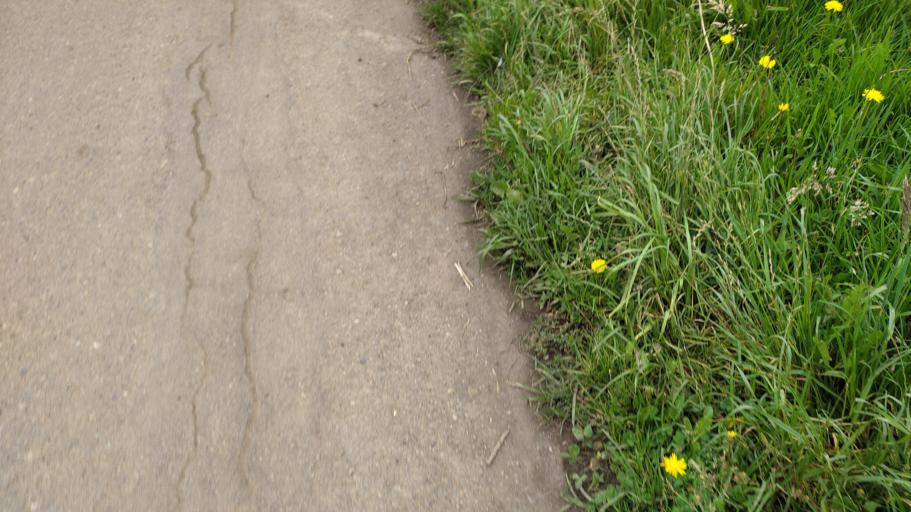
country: EC
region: Chimborazo
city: Riobamba
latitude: -1.6758
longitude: -78.5658
